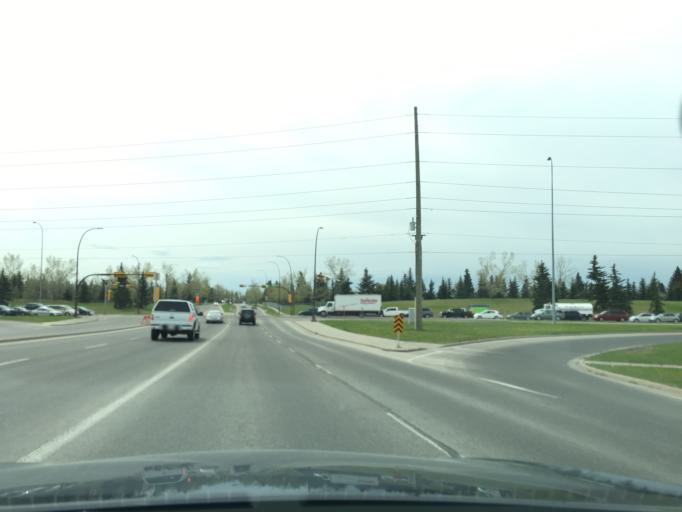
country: CA
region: Alberta
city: Calgary
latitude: 50.9503
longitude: -114.0602
